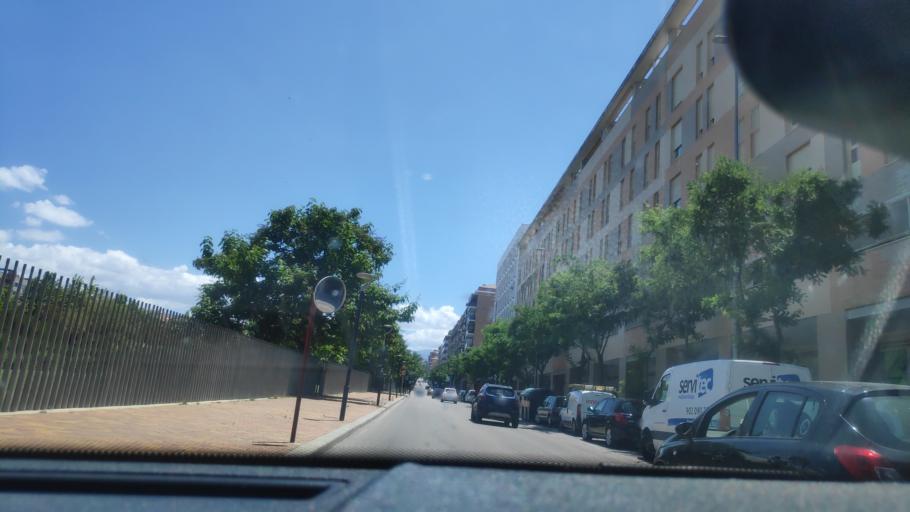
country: ES
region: Andalusia
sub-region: Provincia de Jaen
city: Jaen
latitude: 37.7892
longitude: -3.7919
